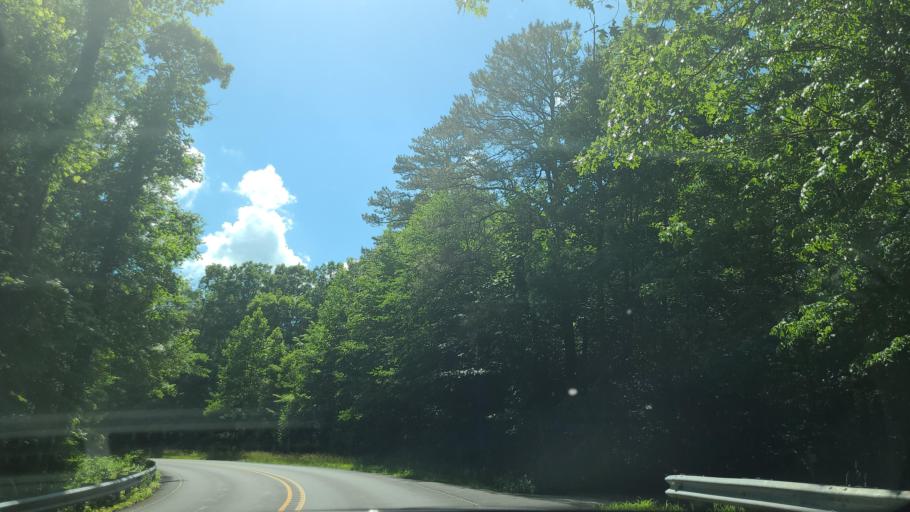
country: US
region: Kentucky
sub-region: Whitley County
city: Williamsburg
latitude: 36.8446
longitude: -84.3173
